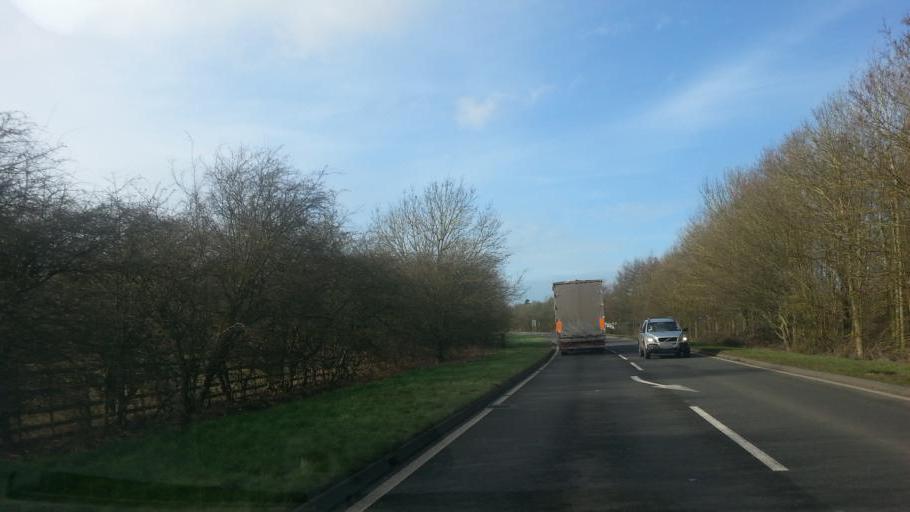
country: GB
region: England
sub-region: District of Rutland
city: Ridlington
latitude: 52.5960
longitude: -0.7856
